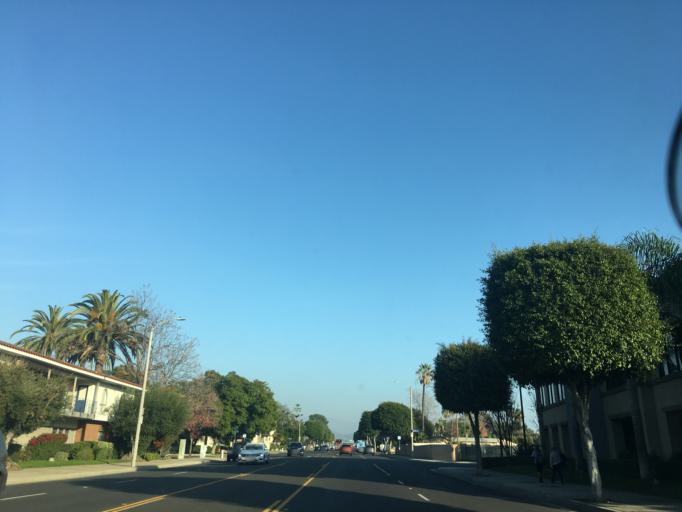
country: US
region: California
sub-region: Orange County
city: Orange
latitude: 33.7878
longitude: -117.8422
